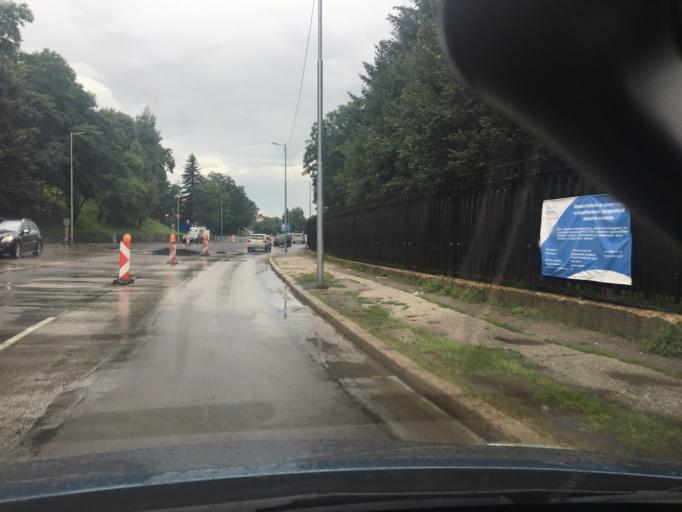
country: BG
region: Sofia-Capital
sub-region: Stolichna Obshtina
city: Sofia
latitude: 42.6487
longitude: 23.2683
